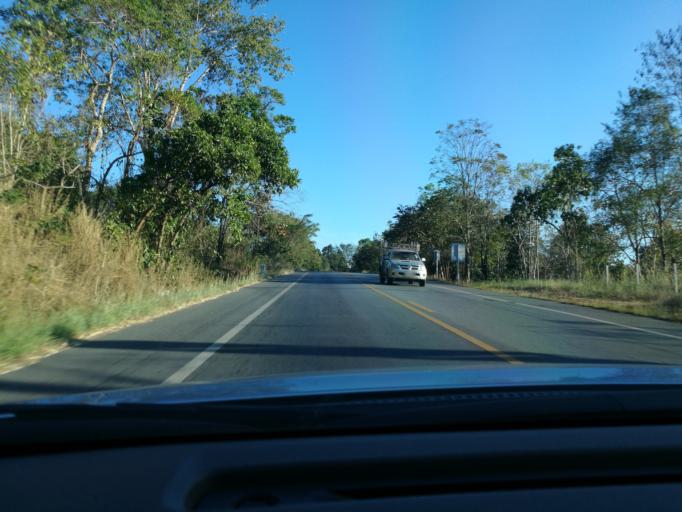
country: TH
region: Phitsanulok
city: Nakhon Thai
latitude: 17.0362
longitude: 100.8173
